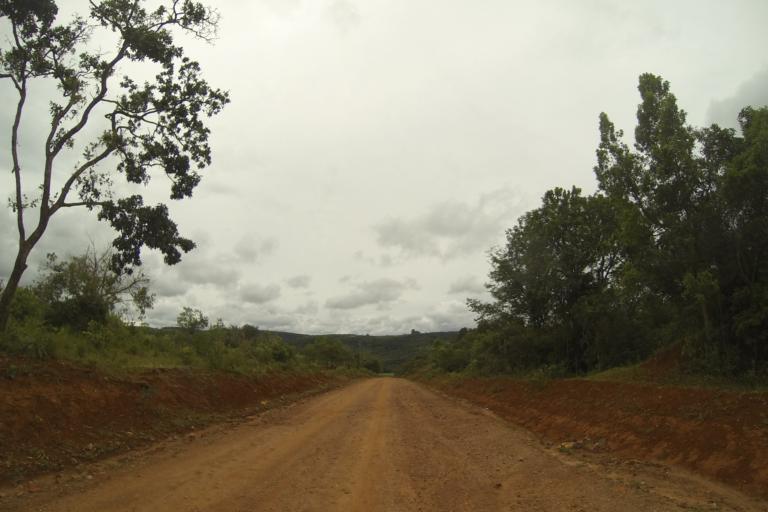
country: BR
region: Minas Gerais
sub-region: Ibia
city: Ibia
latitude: -19.6616
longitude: -46.7012
